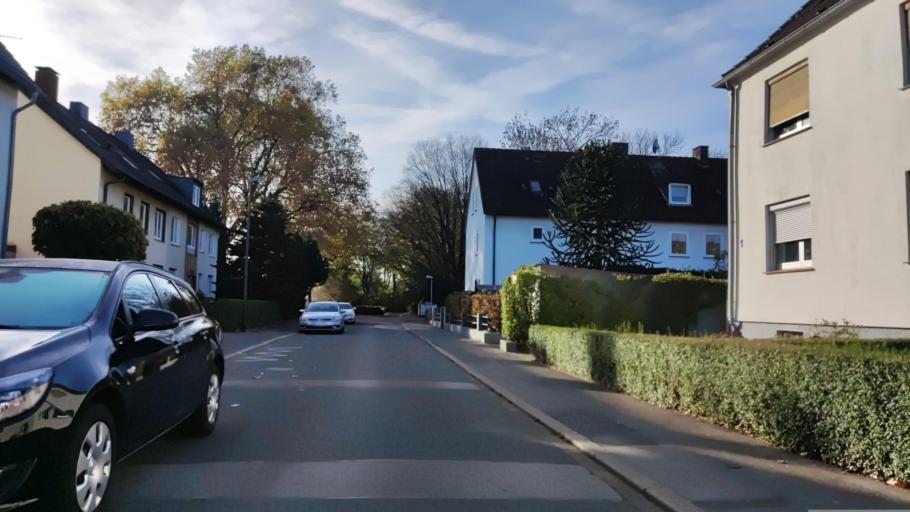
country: DE
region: North Rhine-Westphalia
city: Bochum-Hordel
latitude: 51.5215
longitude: 7.1841
